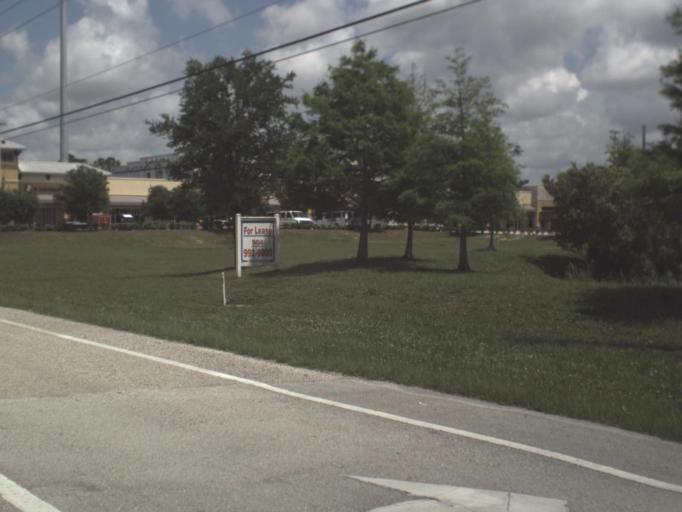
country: US
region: Florida
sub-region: Saint Johns County
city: Palm Valley
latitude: 30.0767
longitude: -81.4504
